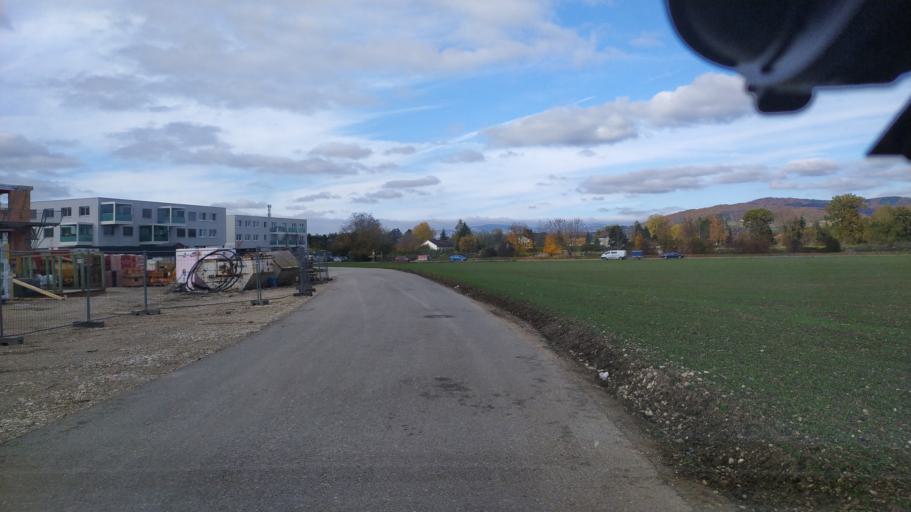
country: AT
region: Upper Austria
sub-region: Politischer Bezirk Urfahr-Umgebung
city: Steyregg
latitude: 48.2547
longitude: 14.3706
